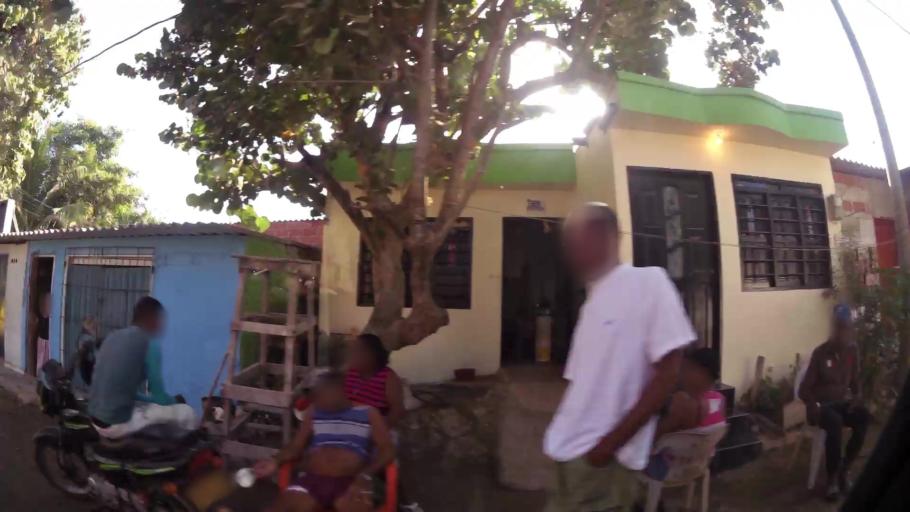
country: CO
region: Bolivar
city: Cartagena
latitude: 10.4840
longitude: -75.4906
